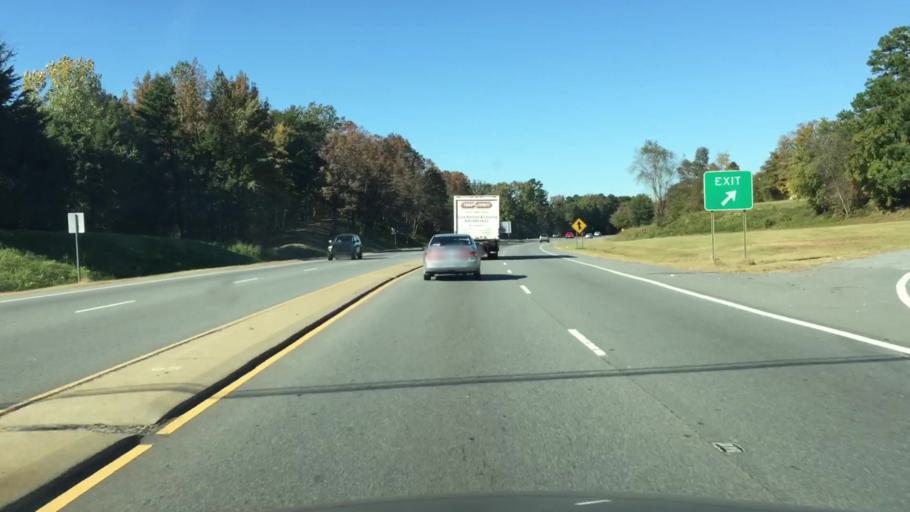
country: US
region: North Carolina
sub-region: Rowan County
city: Salisbury
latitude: 35.6527
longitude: -80.4993
